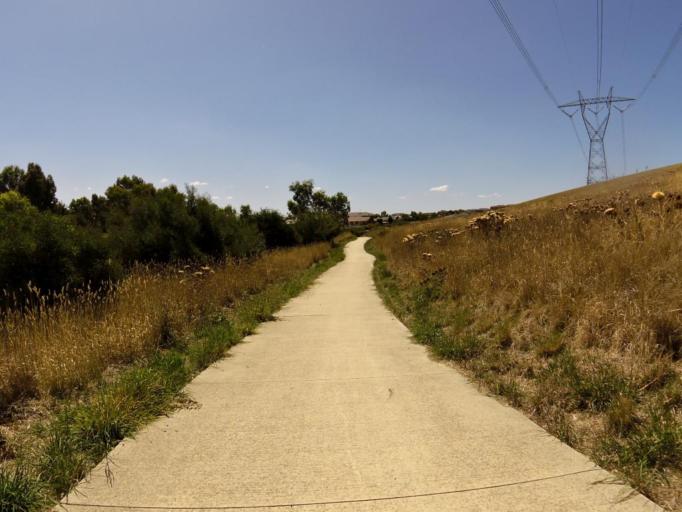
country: AU
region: Victoria
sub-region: Hume
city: Meadow Heights
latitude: -37.6508
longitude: 144.9086
